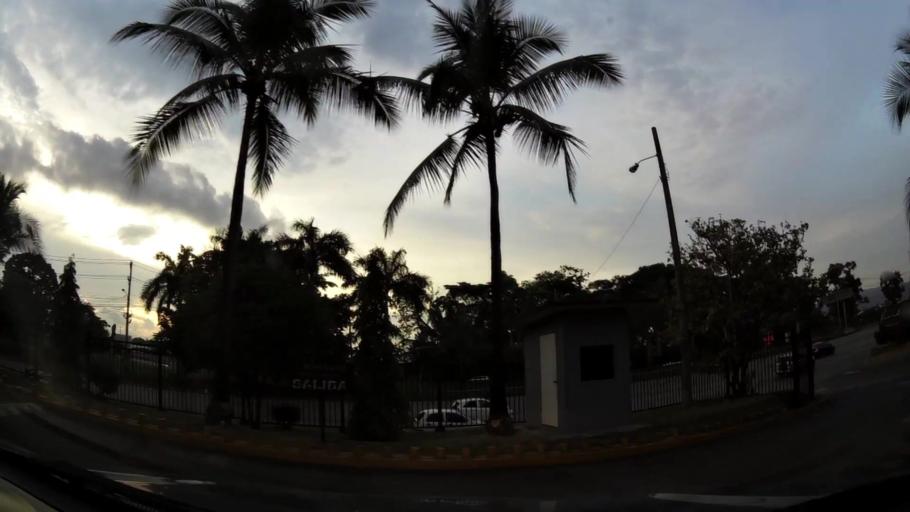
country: PA
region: Panama
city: Tocumen
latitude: 9.0706
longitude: -79.4034
